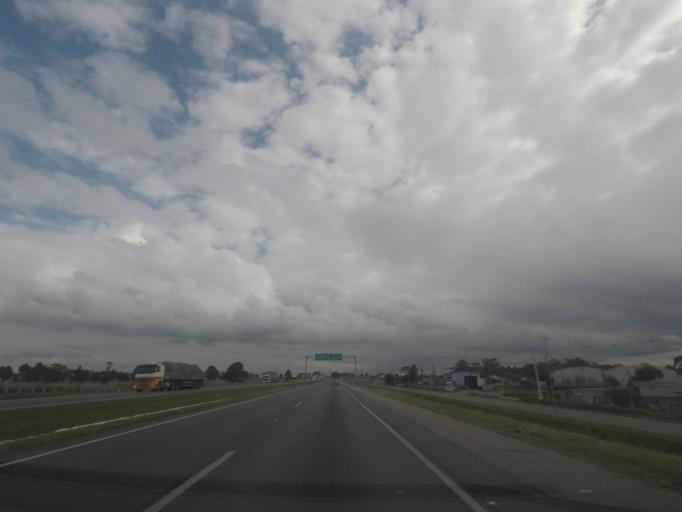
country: BR
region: Parana
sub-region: Piraquara
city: Piraquara
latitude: -25.5056
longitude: -49.1237
